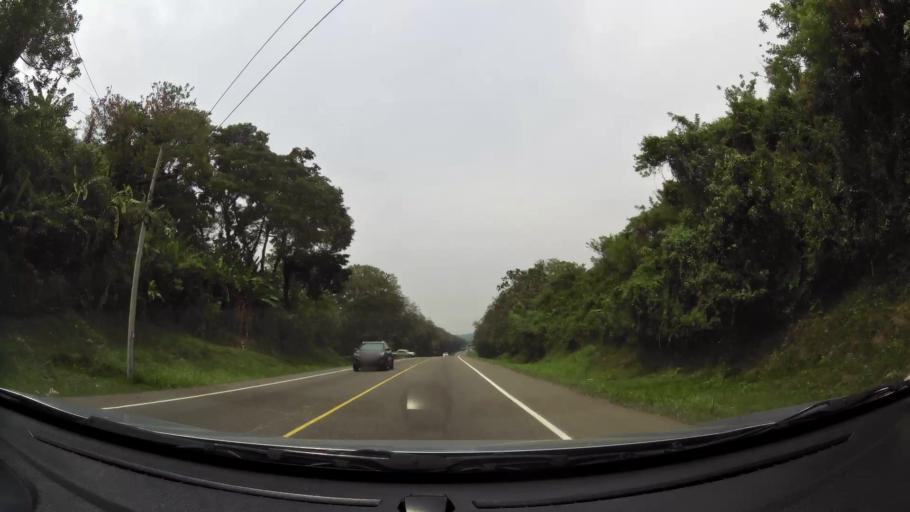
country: HN
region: Cortes
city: La Guama
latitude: 14.8669
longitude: -87.9498
